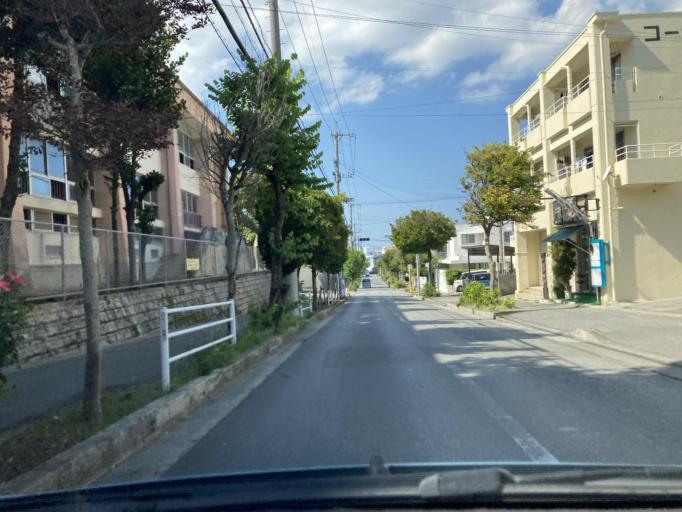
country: JP
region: Okinawa
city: Naha-shi
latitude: 26.1999
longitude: 127.6932
